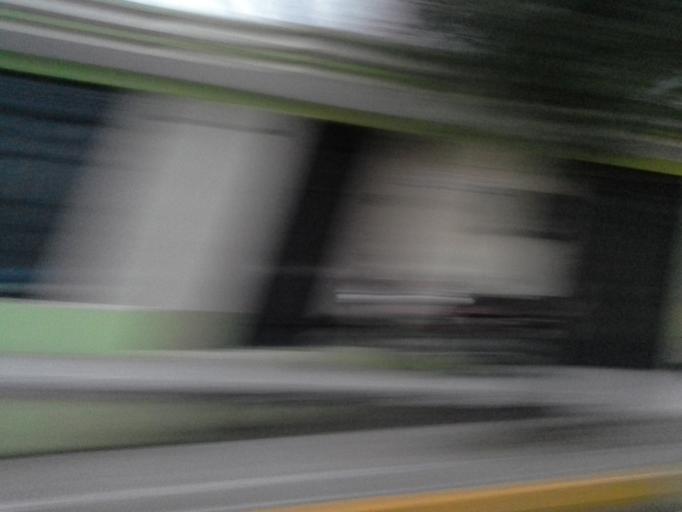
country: CO
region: Caqueta
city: Florencia
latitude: 1.6239
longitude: -75.6046
